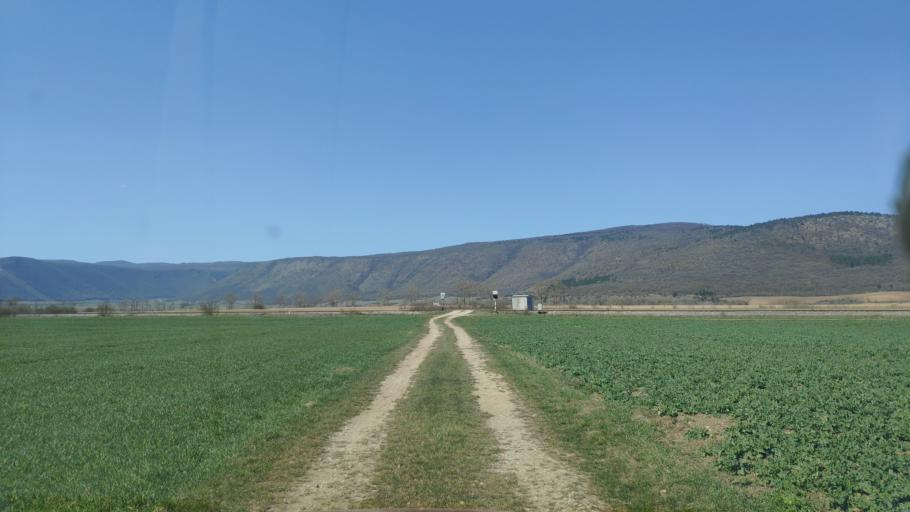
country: SK
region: Kosicky
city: Moldava nad Bodvou
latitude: 48.6039
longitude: 20.9272
